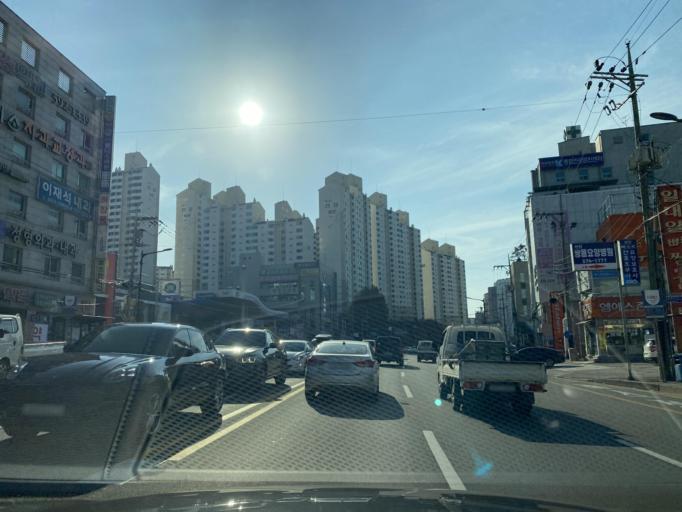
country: KR
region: Chungcheongnam-do
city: Cheonan
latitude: 36.7944
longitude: 127.1265
